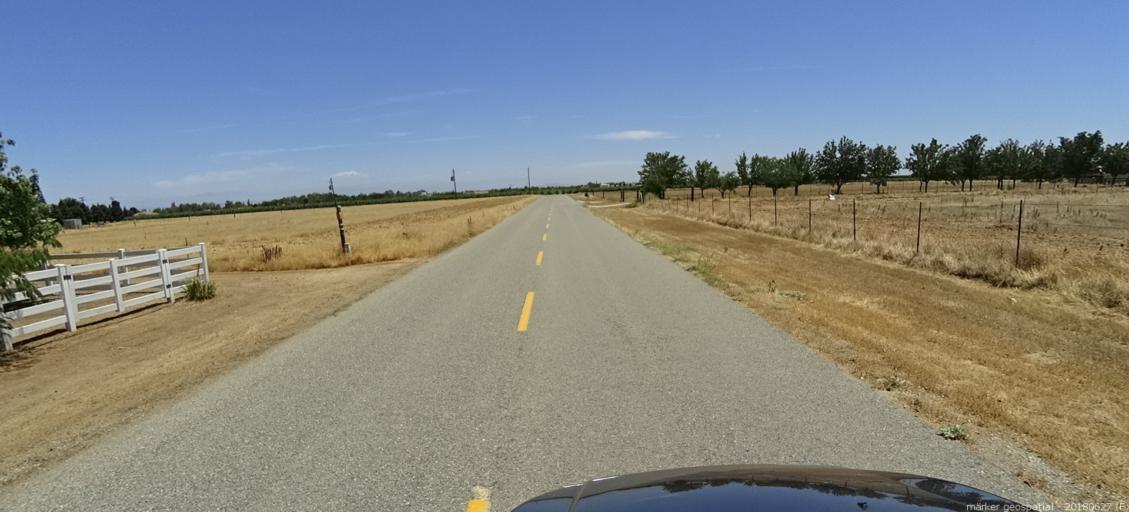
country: US
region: California
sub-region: Madera County
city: Bonadelle Ranchos-Madera Ranchos
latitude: 36.9269
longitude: -119.9150
